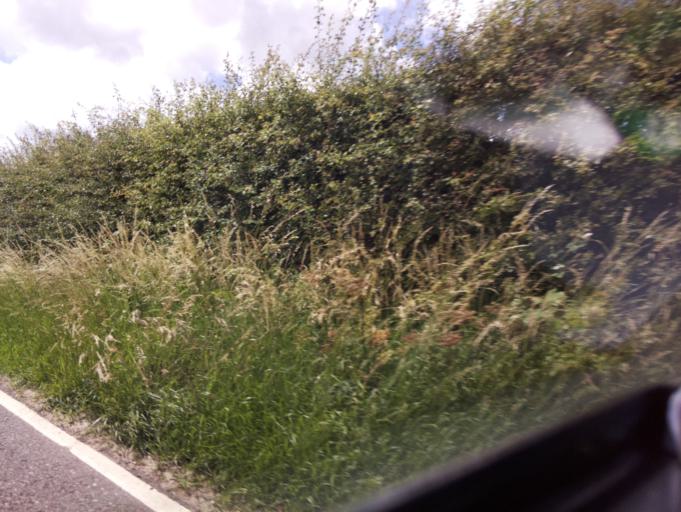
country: GB
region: England
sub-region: Nottinghamshire
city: Burton Joyce
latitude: 53.0075
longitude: -1.0289
